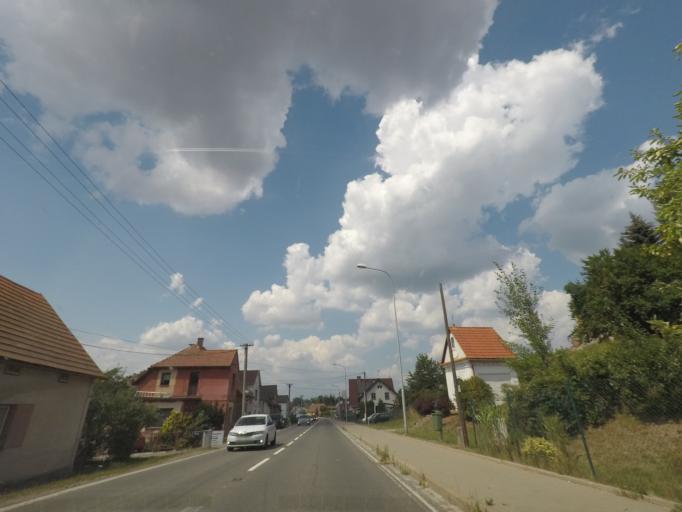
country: CZ
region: Kralovehradecky
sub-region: Okres Trutnov
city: Trutnov
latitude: 50.5583
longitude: 15.8836
